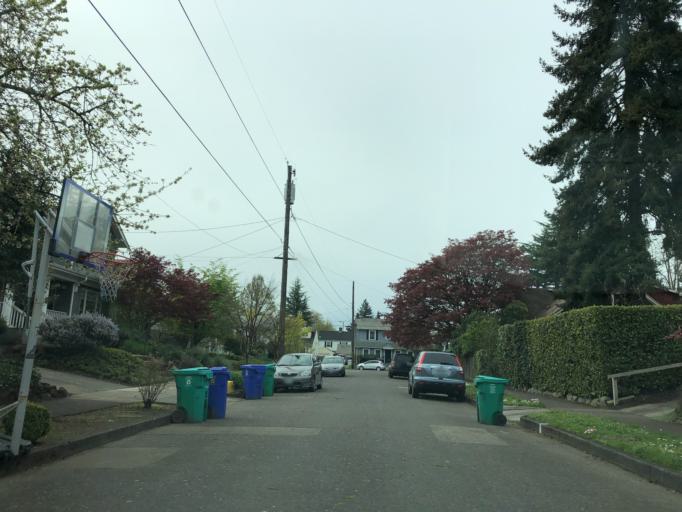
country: US
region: Oregon
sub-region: Multnomah County
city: Portland
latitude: 45.5505
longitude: -122.6297
